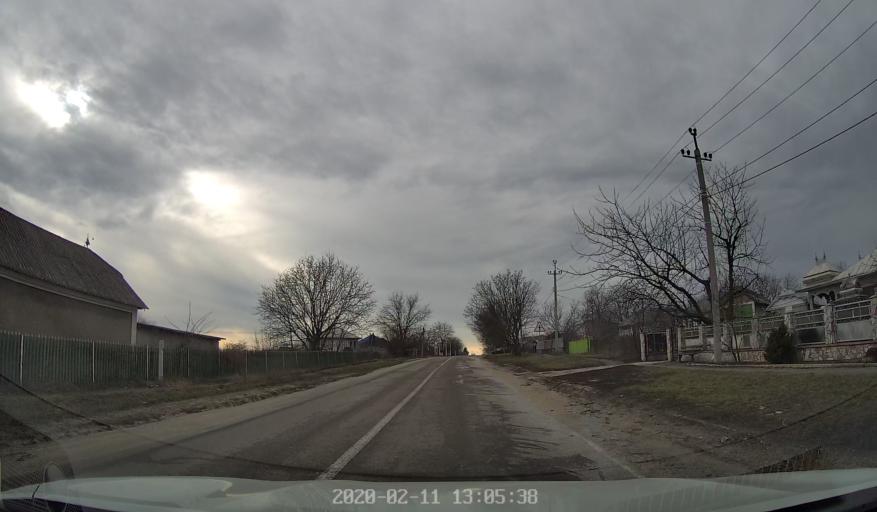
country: RO
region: Botosani
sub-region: Comuna Radauti-Prut
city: Miorcani
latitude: 48.2952
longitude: 26.9314
